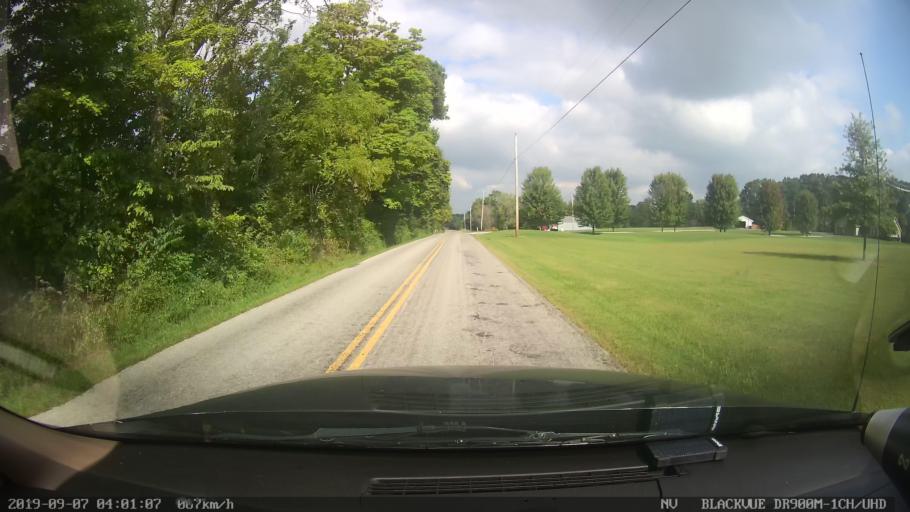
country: US
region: Ohio
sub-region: Licking County
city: Johnstown
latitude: 40.1764
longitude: -82.5841
